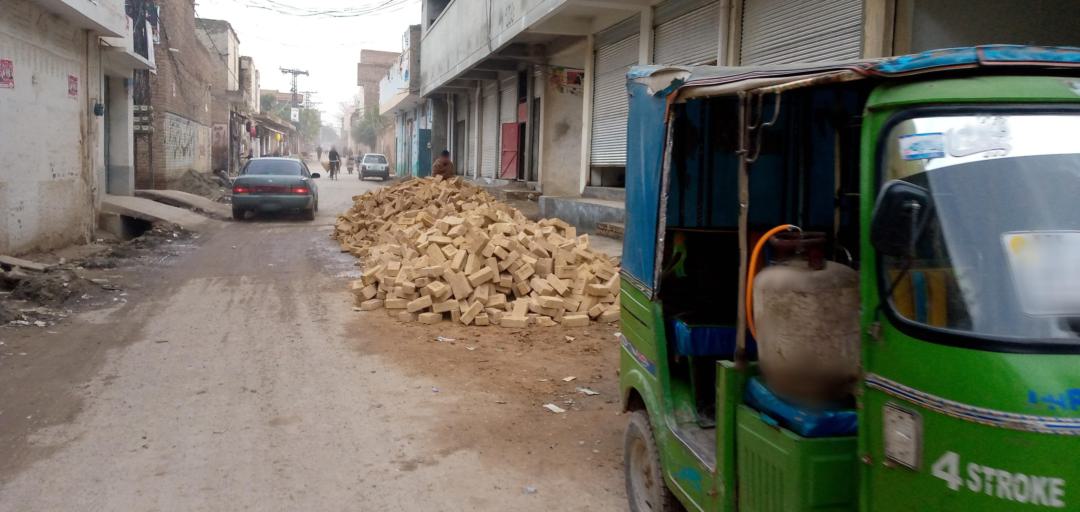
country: PK
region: Khyber Pakhtunkhwa
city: Peshawar
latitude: 34.0162
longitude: 71.5001
